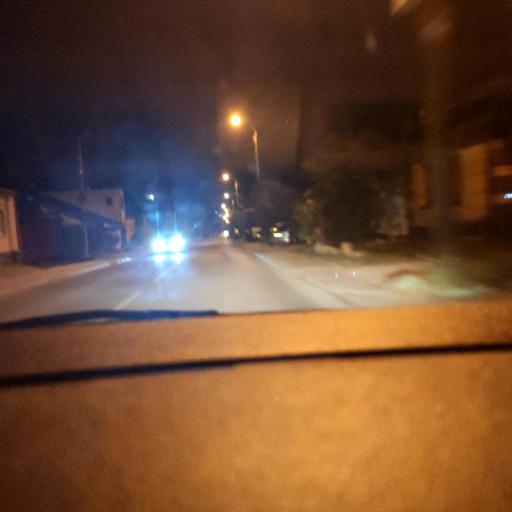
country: RU
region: Voronezj
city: Voronezh
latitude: 51.6525
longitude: 39.2039
